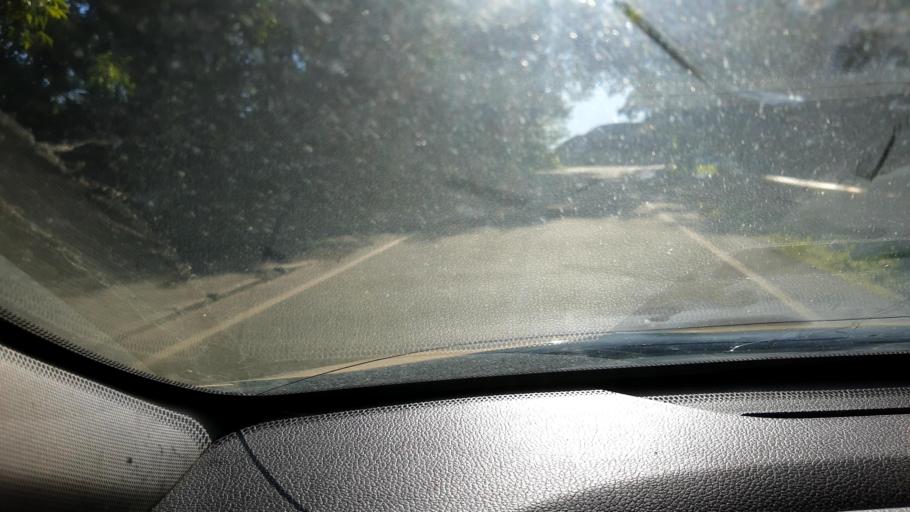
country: RU
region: Moskovskaya
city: Vatutinki
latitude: 55.5040
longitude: 37.3187
